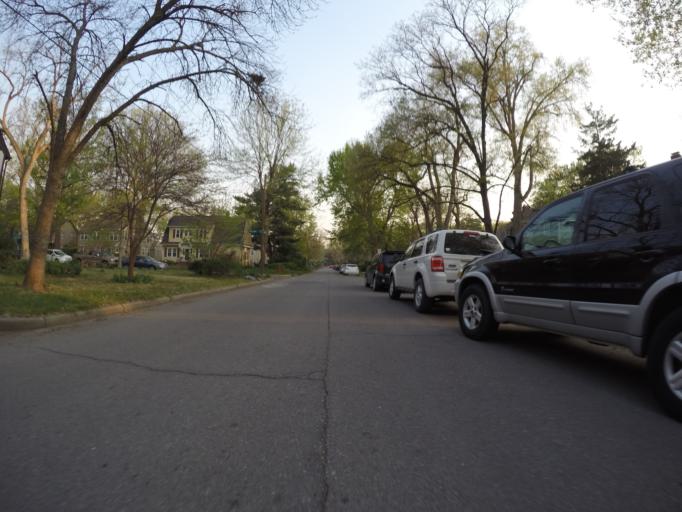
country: US
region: Kansas
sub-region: Riley County
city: Manhattan
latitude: 39.1834
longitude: -96.5854
